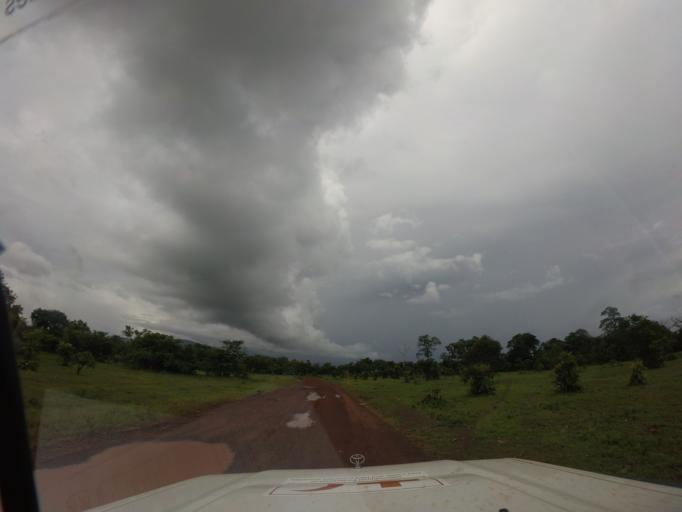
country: SL
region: Northern Province
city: Loma
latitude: 9.8755
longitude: -12.4376
